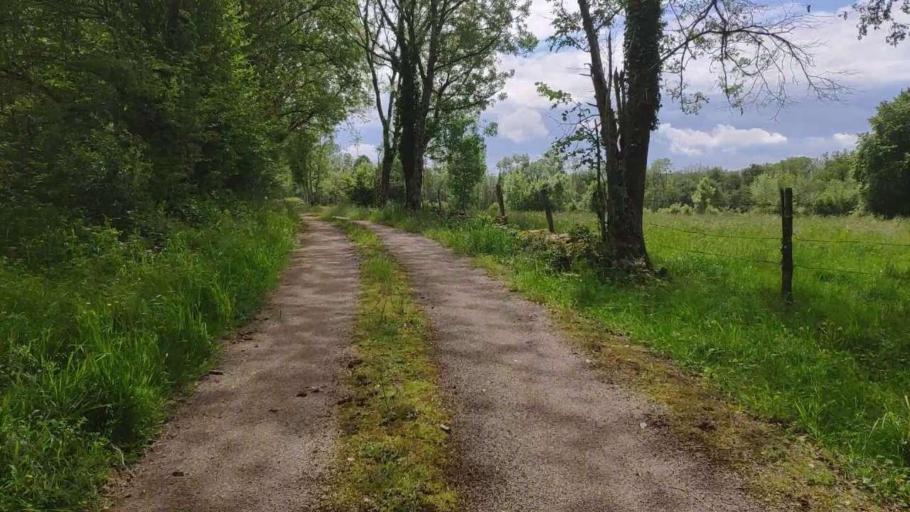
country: FR
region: Franche-Comte
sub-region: Departement du Jura
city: Perrigny
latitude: 46.7423
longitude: 5.6427
